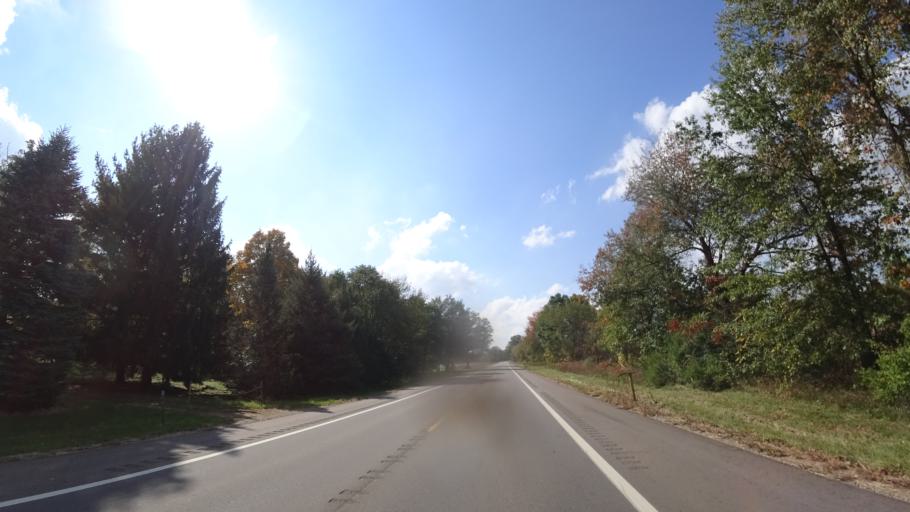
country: US
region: Michigan
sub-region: Calhoun County
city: Athens
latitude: 42.0623
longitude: -85.2046
